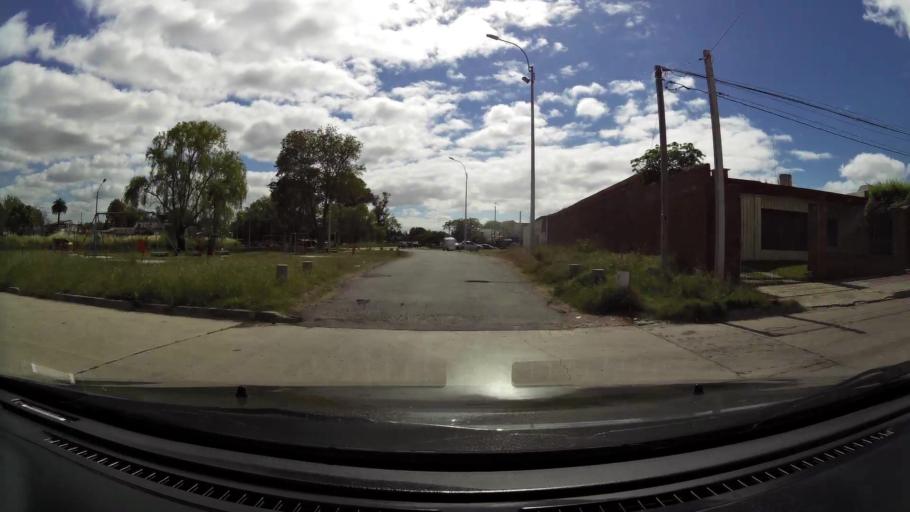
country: UY
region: Canelones
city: Paso de Carrasco
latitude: -34.8841
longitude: -56.1120
